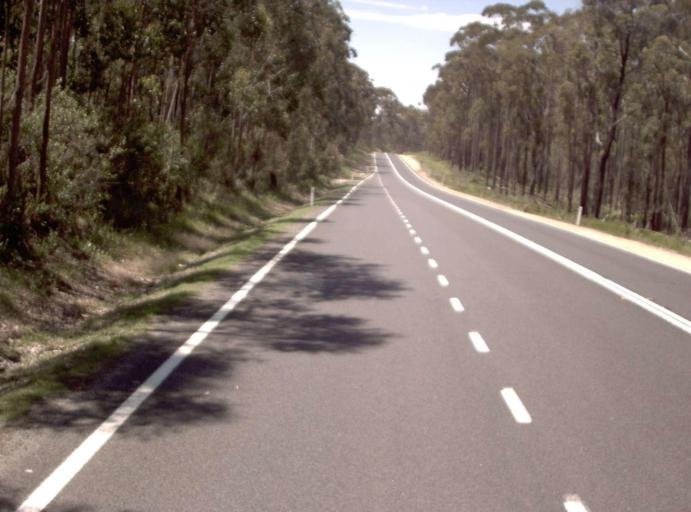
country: AU
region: New South Wales
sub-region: Bombala
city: Bombala
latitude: -37.6483
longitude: 148.8300
